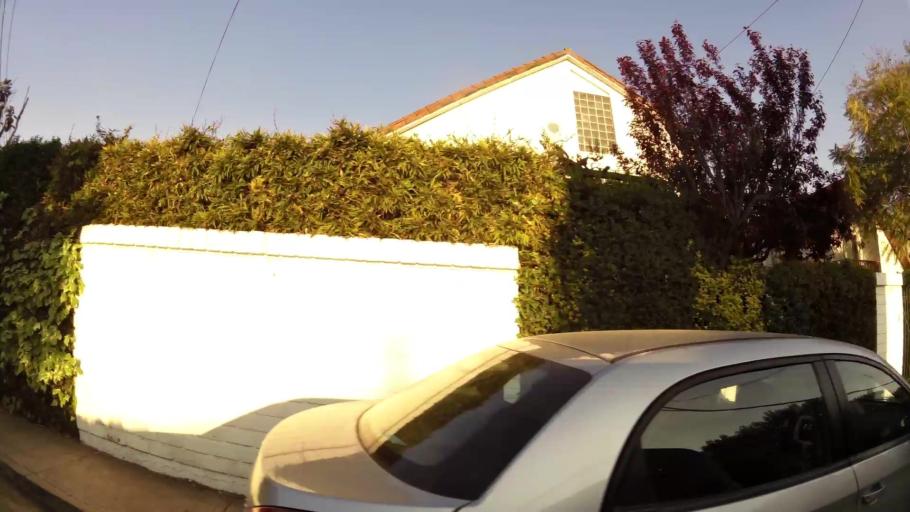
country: CL
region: Santiago Metropolitan
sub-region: Provincia de Santiago
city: Villa Presidente Frei, Nunoa, Santiago, Chile
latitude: -33.4020
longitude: -70.5580
